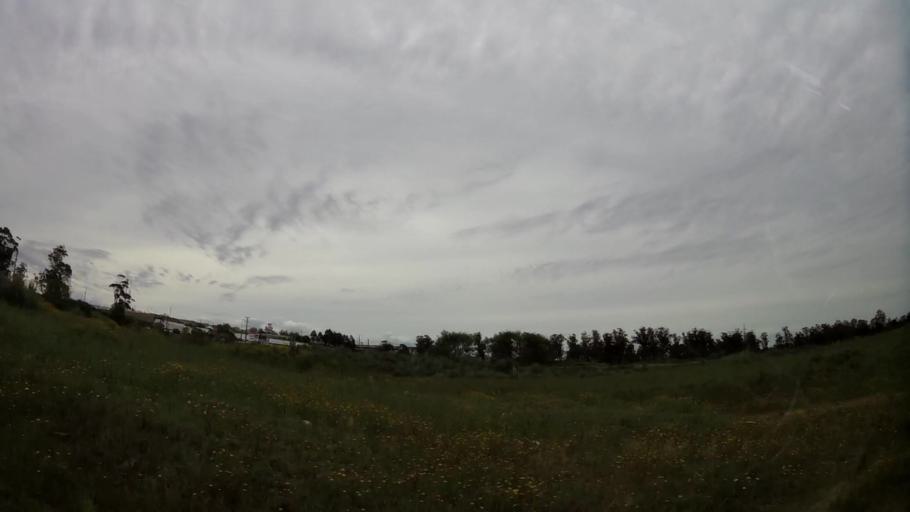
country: UY
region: Maldonado
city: Maldonado
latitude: -34.8866
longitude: -54.9500
